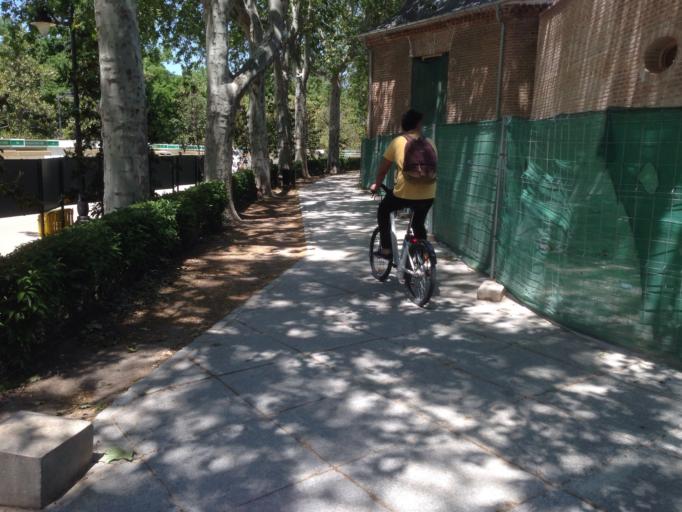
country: ES
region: Madrid
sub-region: Provincia de Madrid
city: Retiro
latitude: 40.4180
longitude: -3.6802
